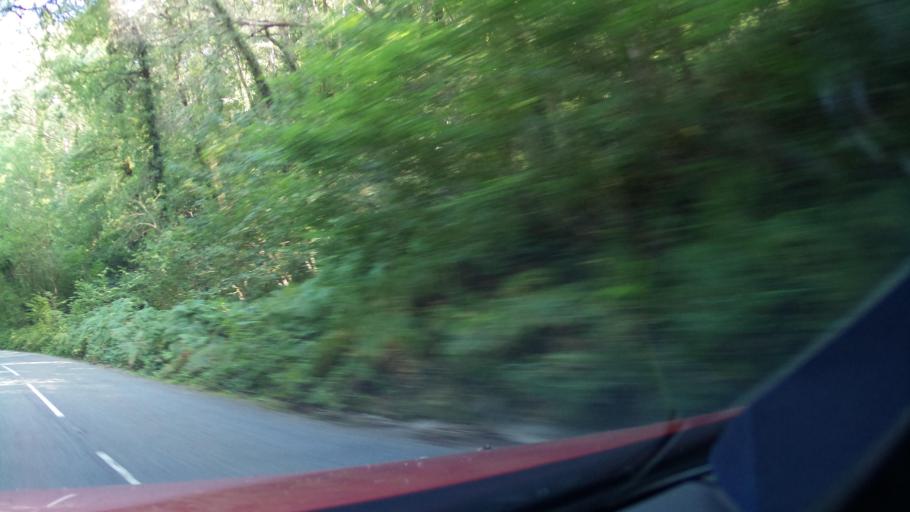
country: GB
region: England
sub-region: Devon
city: Ashburton
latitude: 50.5209
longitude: -3.7957
